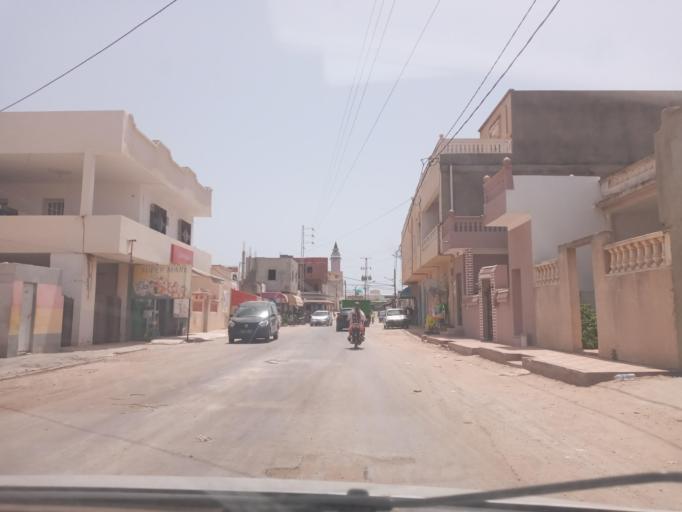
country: TN
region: Nabul
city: El Haouaria
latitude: 37.0126
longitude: 10.9528
